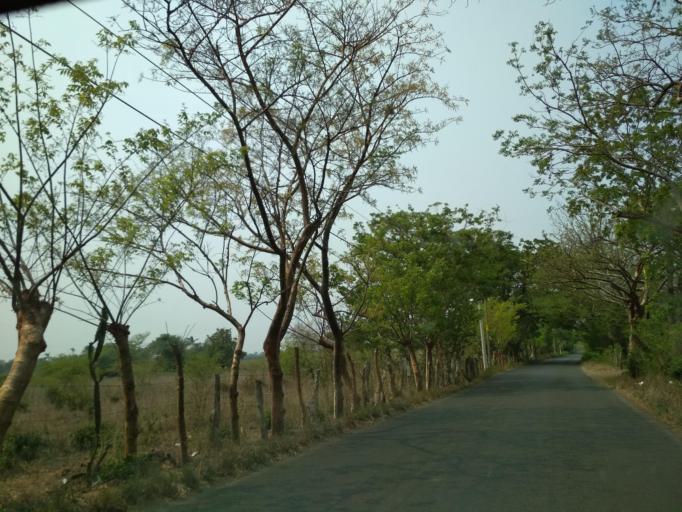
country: MX
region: Veracruz
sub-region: Veracruz
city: Delfino Victoria (Santa Fe)
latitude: 19.2056
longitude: -96.3217
